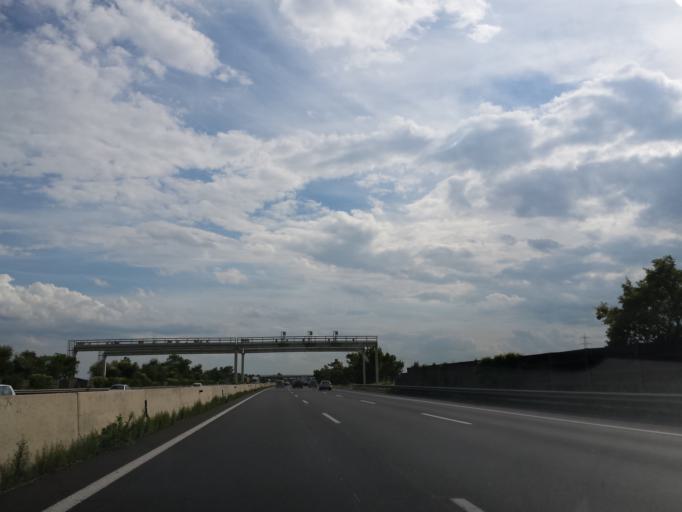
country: AT
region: Lower Austria
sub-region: Politischer Bezirk Wiener Neustadt
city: Felixdorf
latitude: 47.8912
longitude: 16.2067
